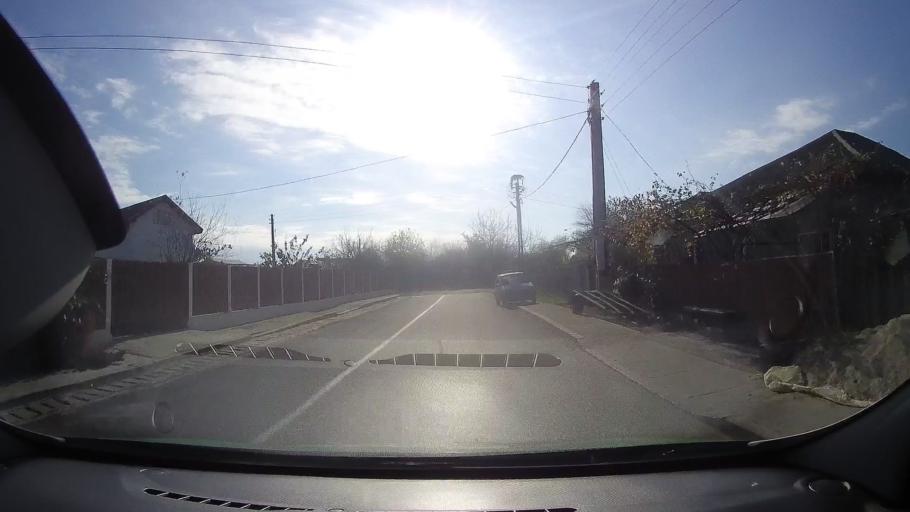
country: RO
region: Tulcea
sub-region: Comuna Murighiol
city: Murighiol
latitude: 45.0373
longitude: 29.1666
